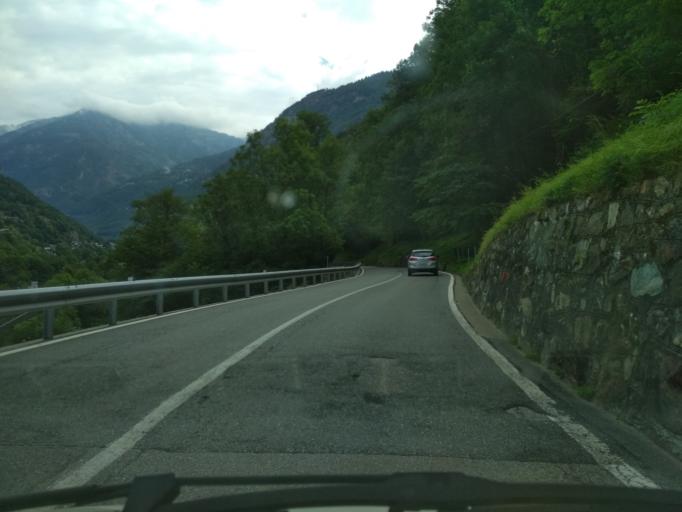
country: IT
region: Aosta Valley
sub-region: Valle d'Aosta
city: Lillianes
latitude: 45.6245
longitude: 7.8299
